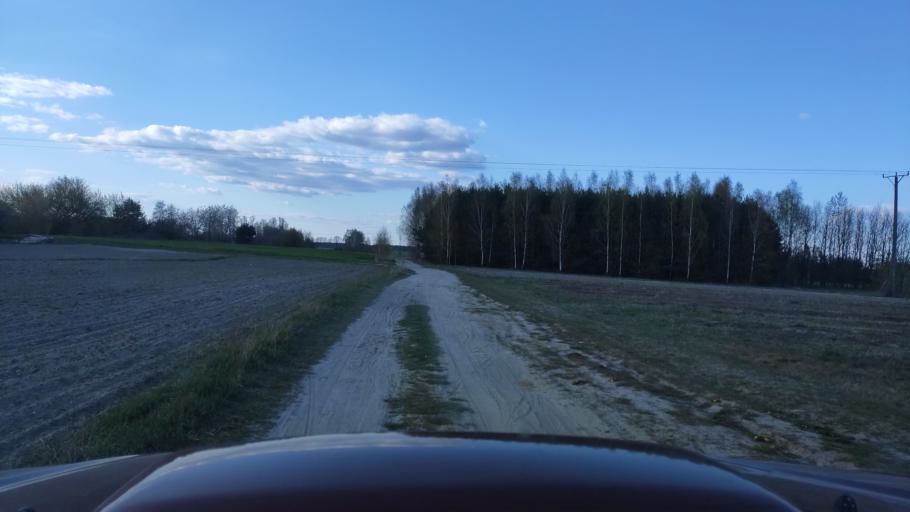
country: PL
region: Masovian Voivodeship
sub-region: Powiat zwolenski
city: Zwolen
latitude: 51.3675
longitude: 21.5751
